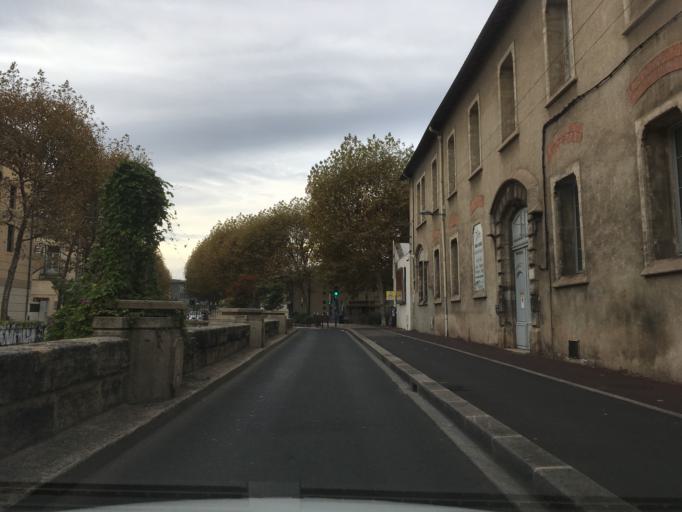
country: FR
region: Languedoc-Roussillon
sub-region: Departement de l'Herault
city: Montpellier
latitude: 43.6151
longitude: 3.8797
